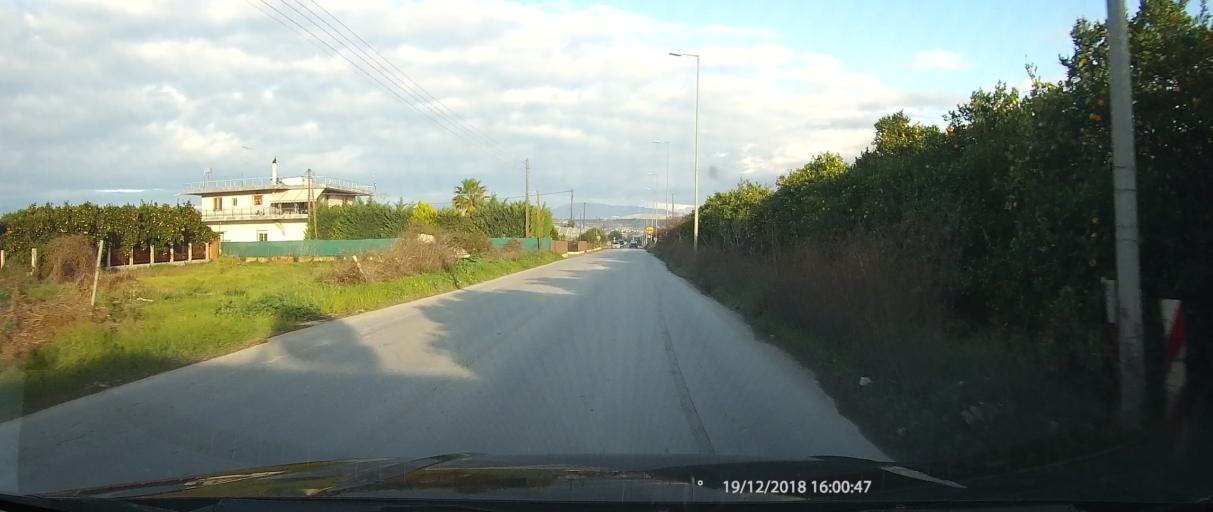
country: GR
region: Peloponnese
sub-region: Nomos Lakonias
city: Skala
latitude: 36.8549
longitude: 22.6804
